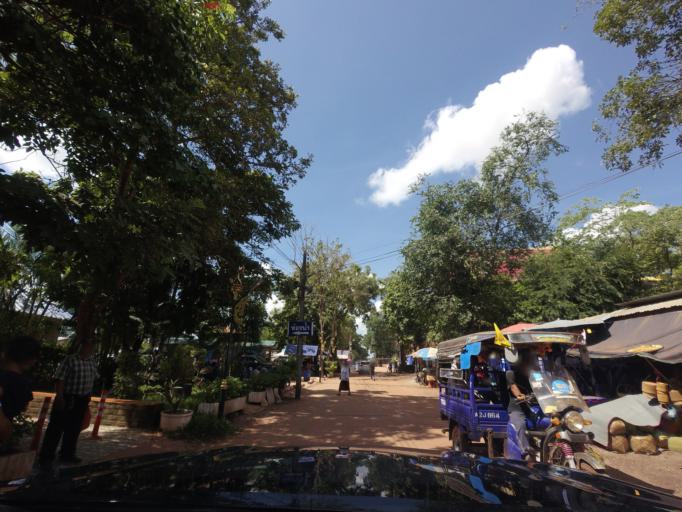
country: TH
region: Changwat Udon Thani
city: Ban Dung
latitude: 17.7425
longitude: 103.3586
